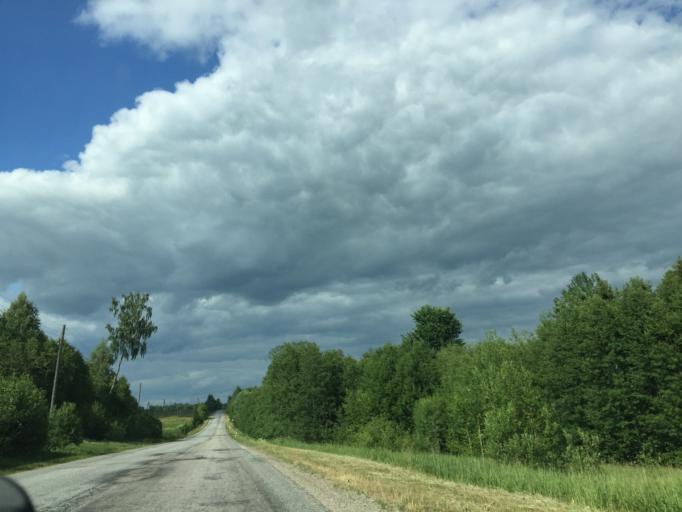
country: LV
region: Skriveri
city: Skriveri
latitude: 56.8136
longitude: 25.1158
